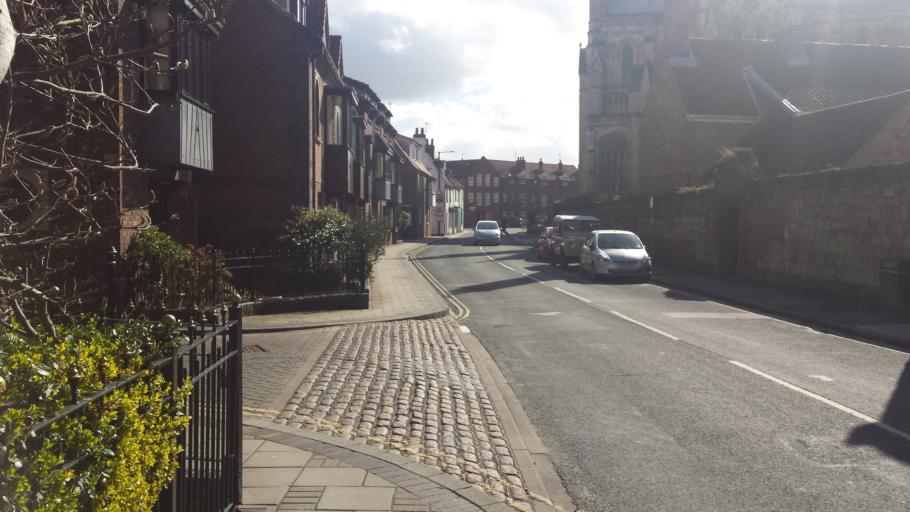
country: GB
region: England
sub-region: East Riding of Yorkshire
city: Beverley
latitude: 53.8402
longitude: -0.4246
